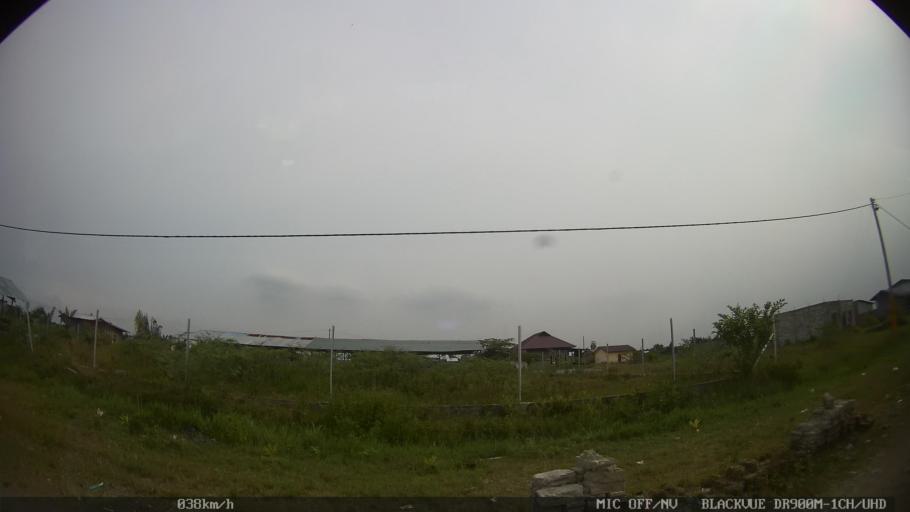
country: ID
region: North Sumatra
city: Medan
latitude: 3.5732
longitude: 98.7511
